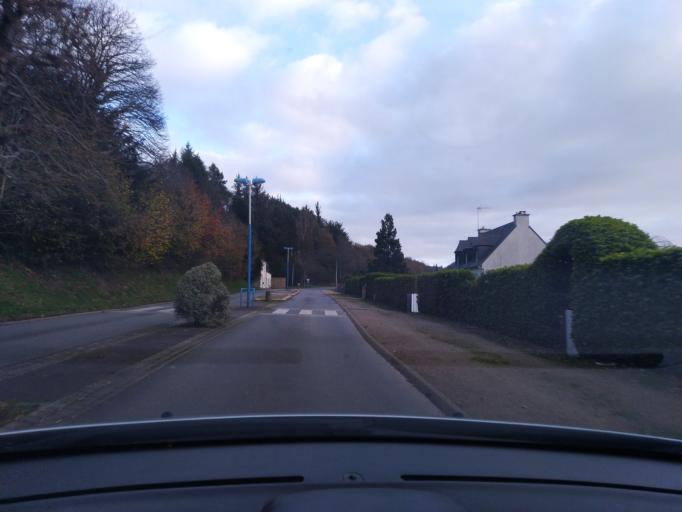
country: FR
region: Brittany
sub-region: Departement du Finistere
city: Plouigneau
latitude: 48.5639
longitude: -3.6352
